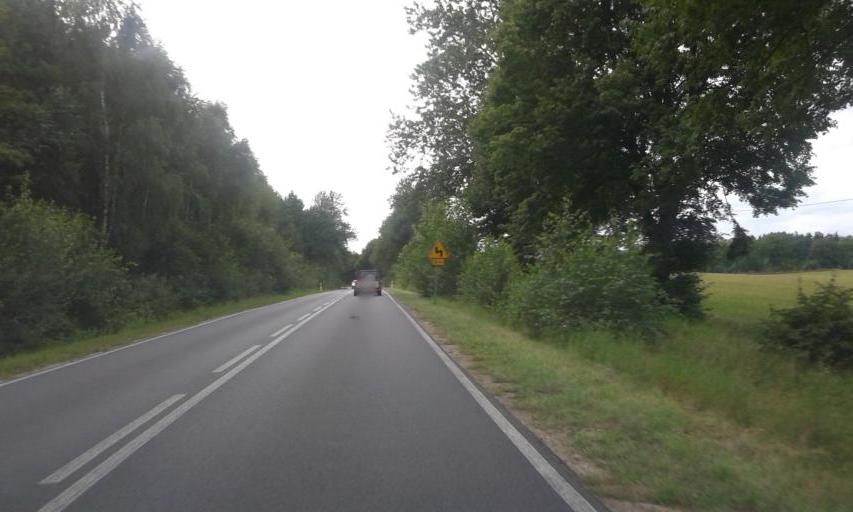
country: PL
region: West Pomeranian Voivodeship
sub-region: Powiat szczecinecki
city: Szczecinek
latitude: 53.7167
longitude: 16.5635
